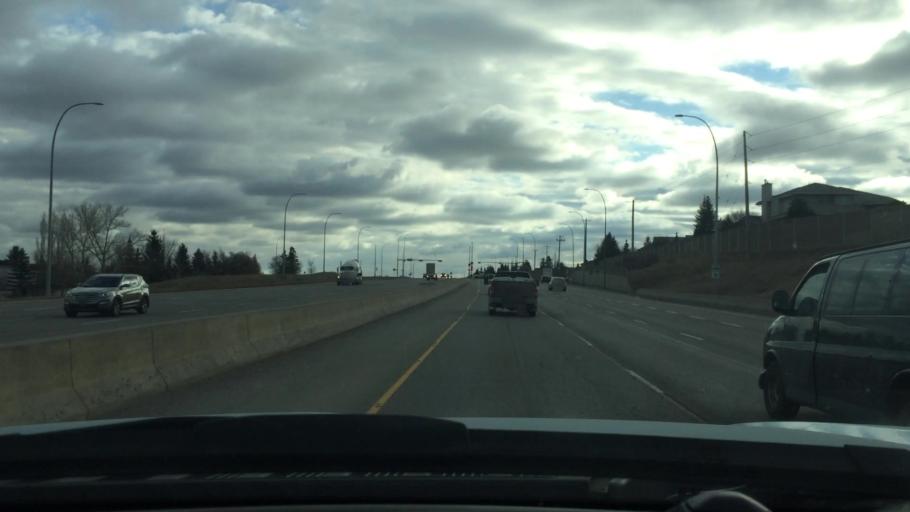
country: CA
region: Alberta
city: Calgary
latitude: 51.1396
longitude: -114.0854
